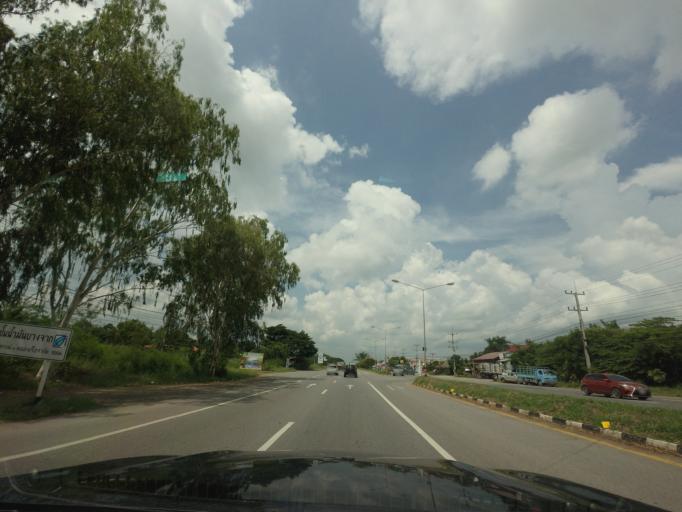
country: TH
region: Khon Kaen
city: Nong Ruea
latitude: 16.4895
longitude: 102.4512
